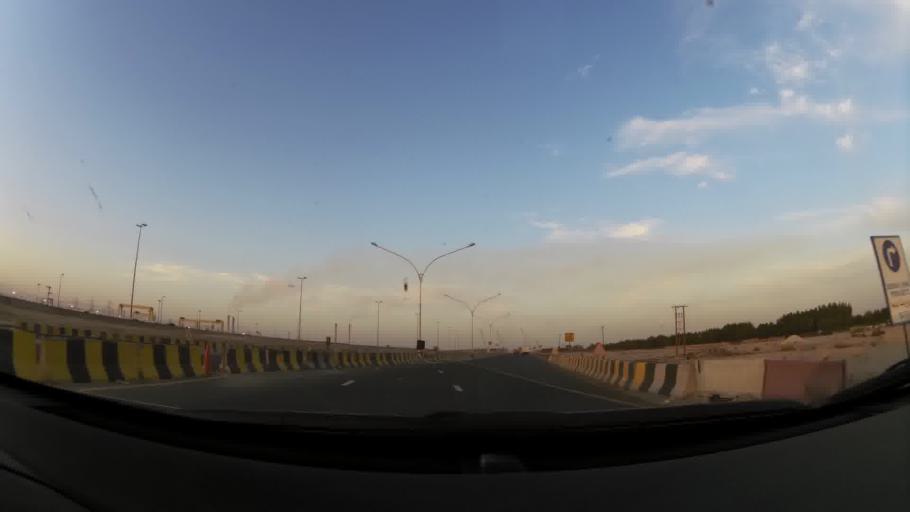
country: KW
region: Al Asimah
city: Ar Rabiyah
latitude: 29.3392
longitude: 47.8008
